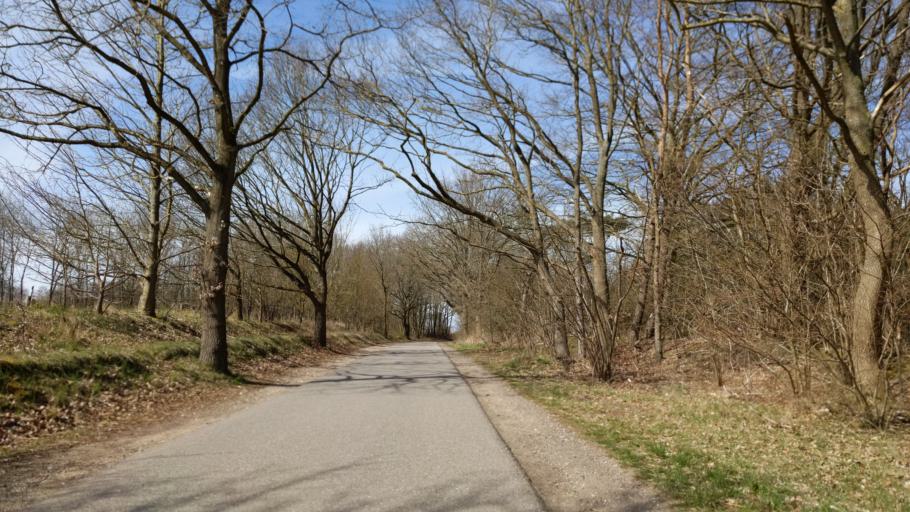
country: DE
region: Schleswig-Holstein
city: Ratekau
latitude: 53.9837
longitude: 10.6809
